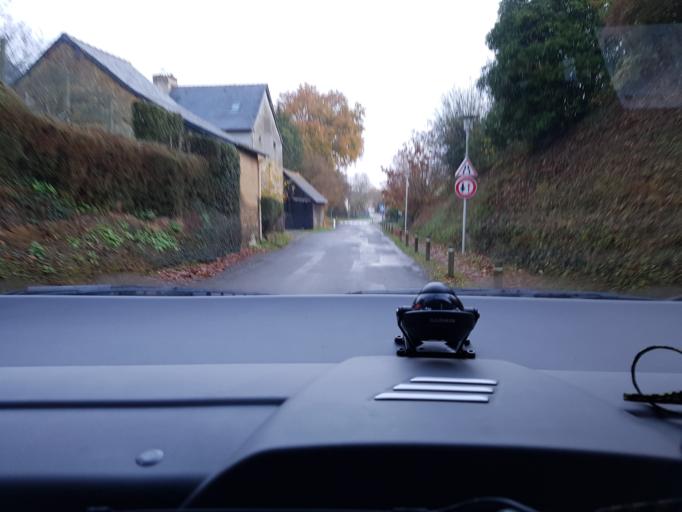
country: FR
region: Brittany
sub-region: Departement d'Ille-et-Vilaine
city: Saint-Sulpice-la-Foret
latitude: 48.2147
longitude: -1.5795
